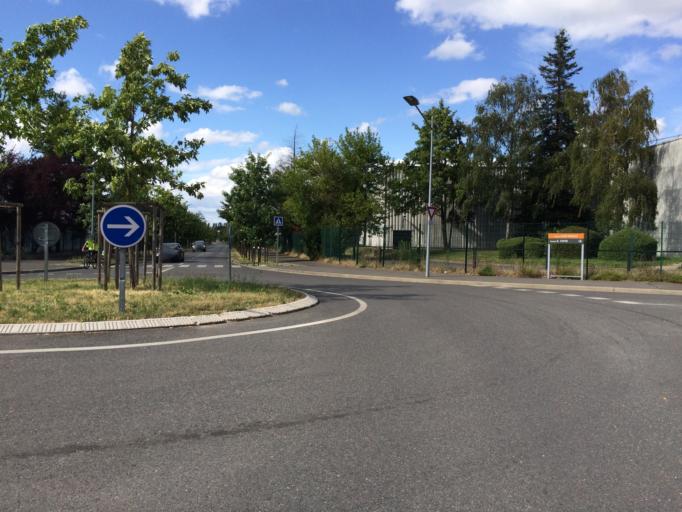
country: FR
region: Ile-de-France
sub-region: Departement de l'Essonne
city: Morangis
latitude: 48.7006
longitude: 2.3390
